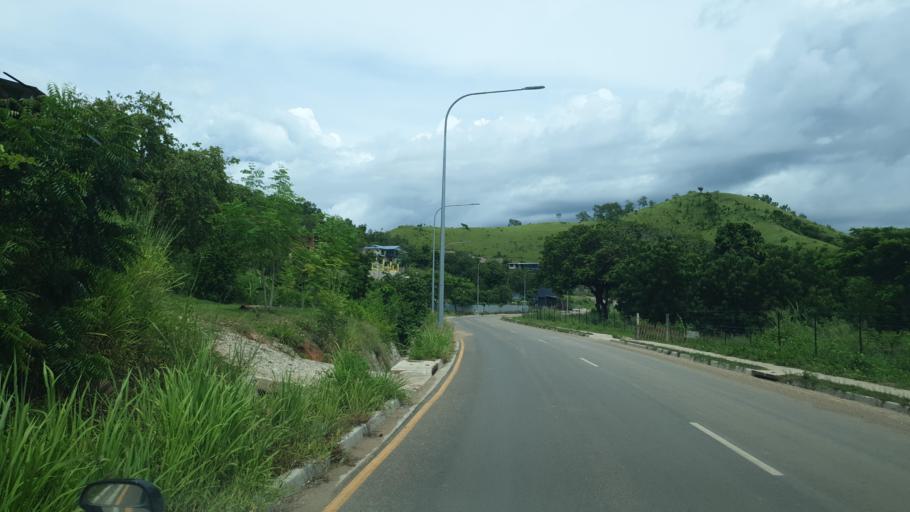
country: PG
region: National Capital
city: Port Moresby
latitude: -9.5281
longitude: 147.2473
